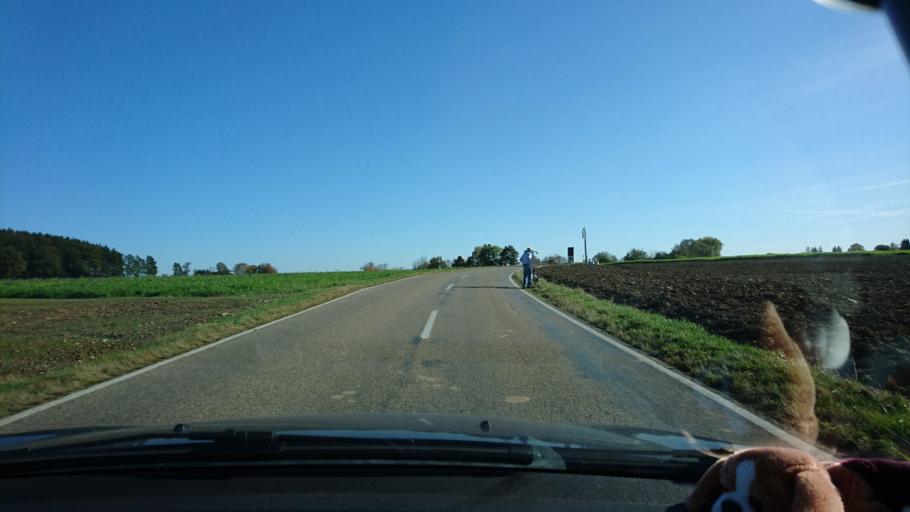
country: DE
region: Bavaria
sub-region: Upper Bavaria
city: Anzing
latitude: 48.1349
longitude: 11.8302
